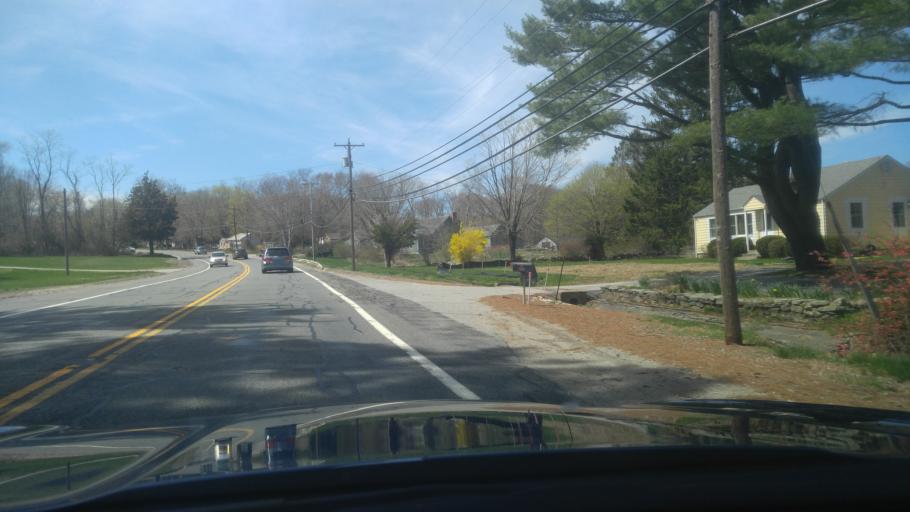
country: US
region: Rhode Island
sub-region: Washington County
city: Exeter
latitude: 41.5765
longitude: -71.5284
